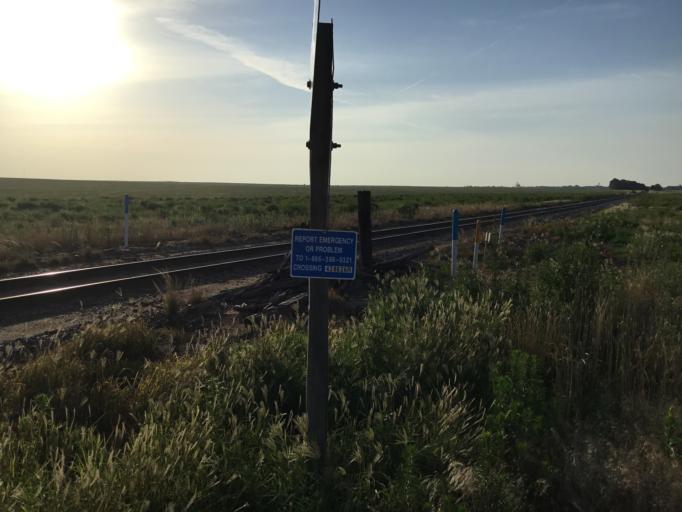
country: US
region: Kansas
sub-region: Sedgwick County
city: Cheney
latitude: 37.4694
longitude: -97.8808
